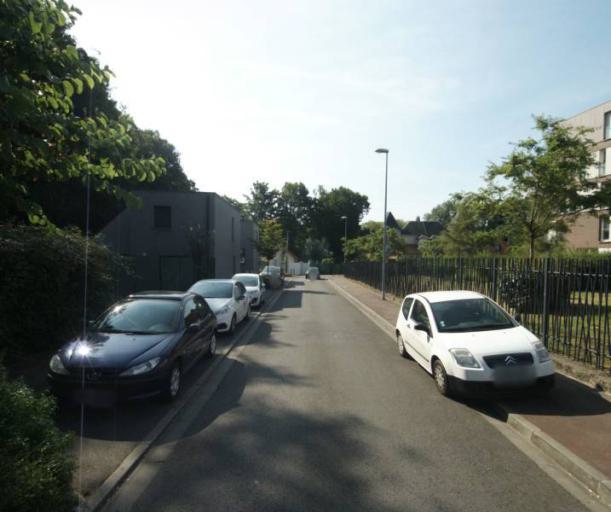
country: FR
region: Nord-Pas-de-Calais
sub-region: Departement du Nord
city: Tourcoing
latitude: 50.7103
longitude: 3.1495
